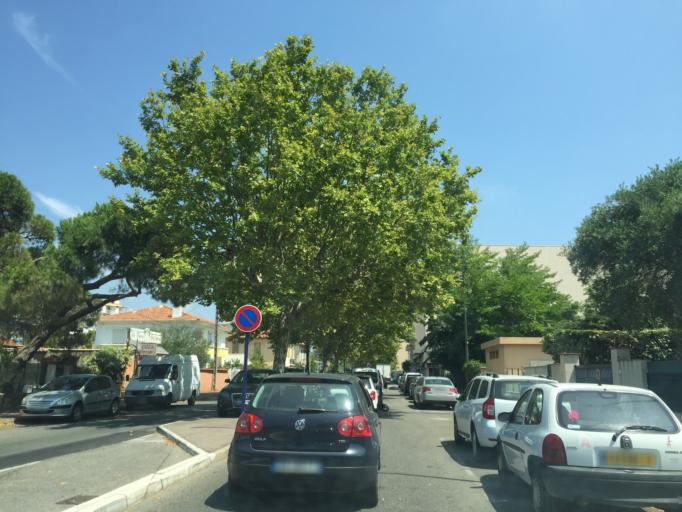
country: FR
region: Provence-Alpes-Cote d'Azur
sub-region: Departement du Var
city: Saint-Raphael
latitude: 43.4262
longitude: 6.7592
